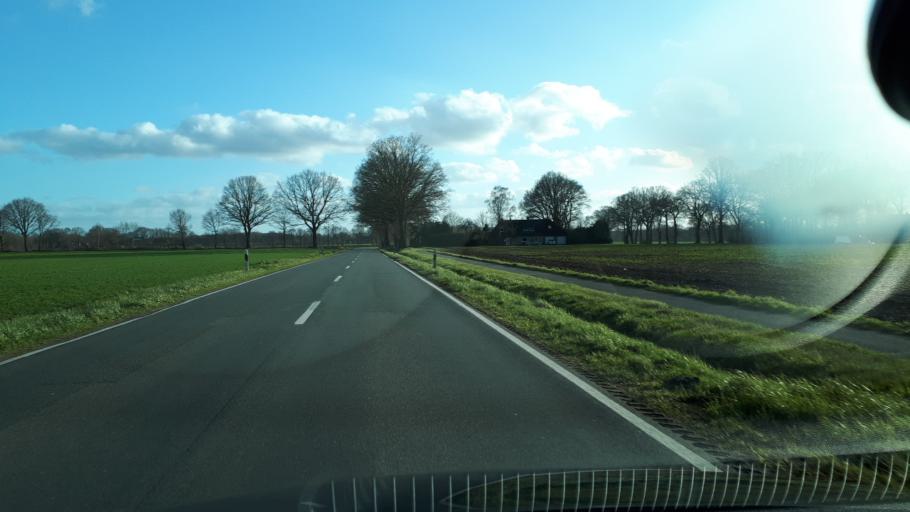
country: DE
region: Lower Saxony
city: Vrees
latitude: 52.8712
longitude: 7.8311
